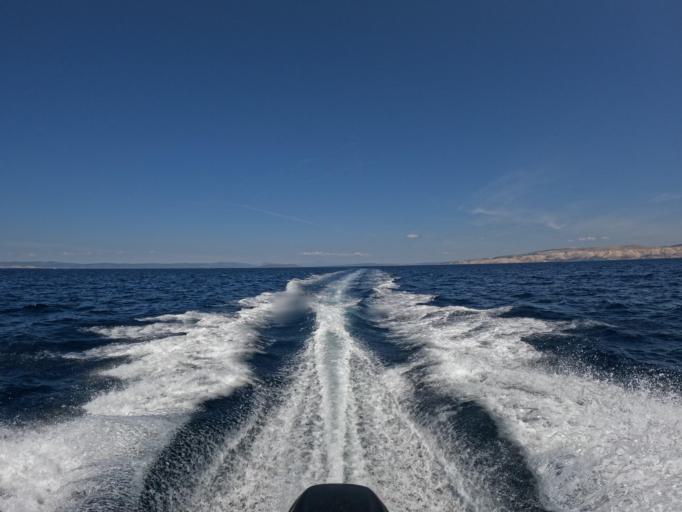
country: HR
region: Primorsko-Goranska
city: Lopar
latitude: 44.8755
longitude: 14.6624
